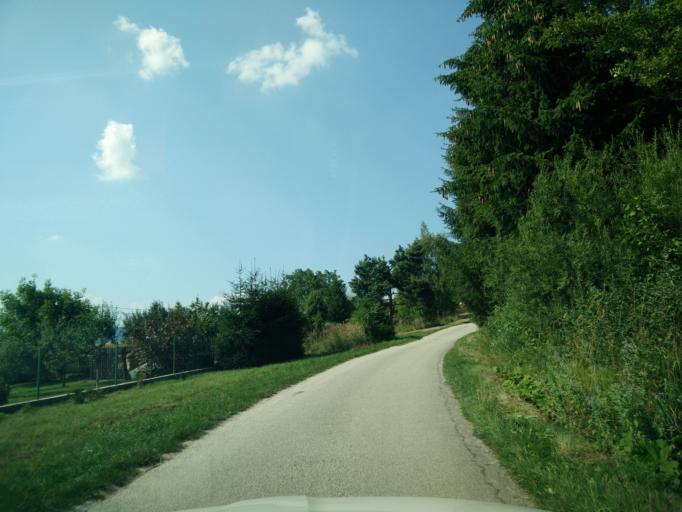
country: SK
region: Zilinsky
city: Rajec
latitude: 49.1033
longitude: 18.7095
